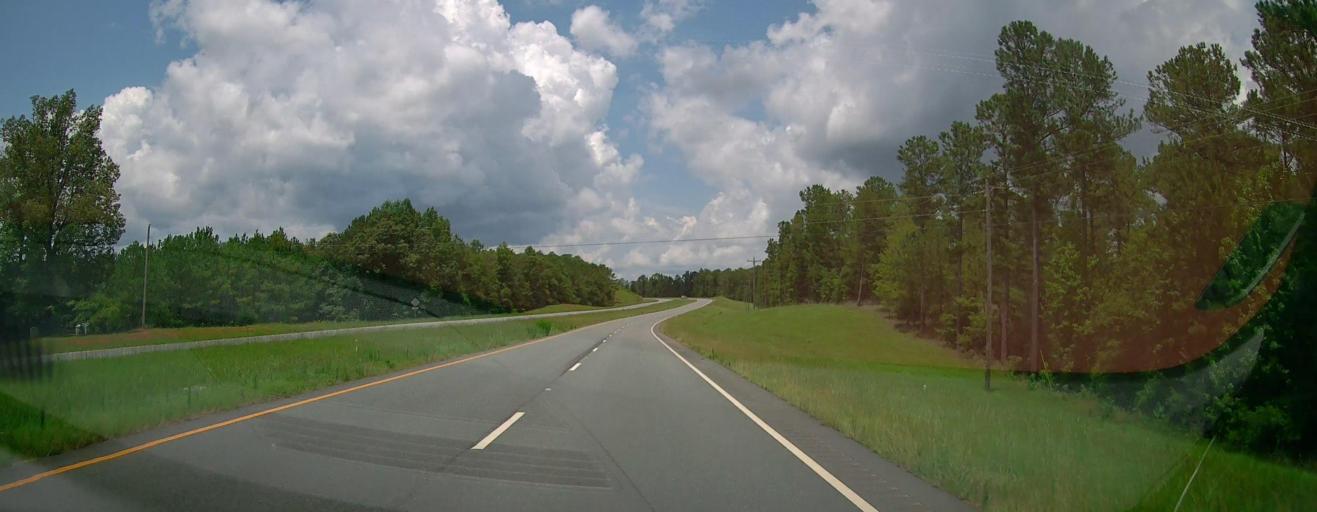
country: US
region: Georgia
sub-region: Upson County
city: Thomaston
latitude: 32.8117
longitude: -84.2854
